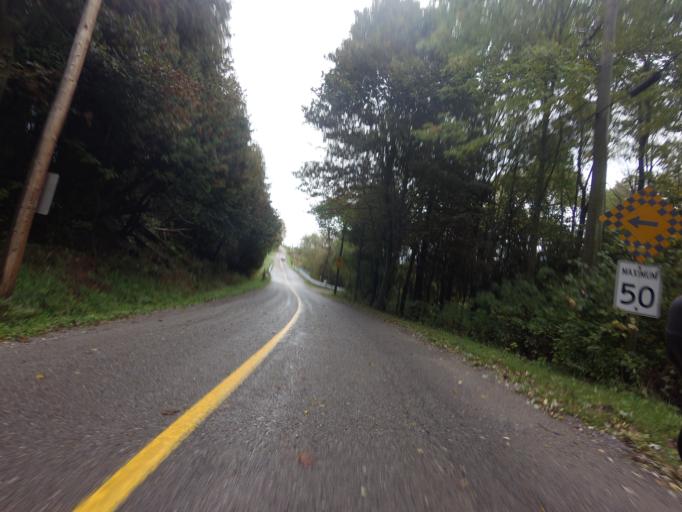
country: CA
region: Ontario
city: Cobourg
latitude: 43.8978
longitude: -78.4842
